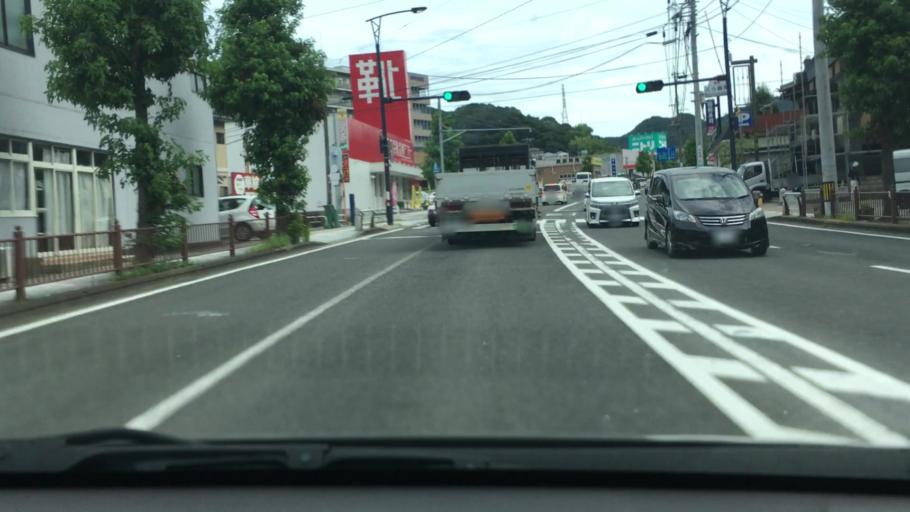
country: JP
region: Nagasaki
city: Togitsu
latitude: 32.8223
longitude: 129.8486
